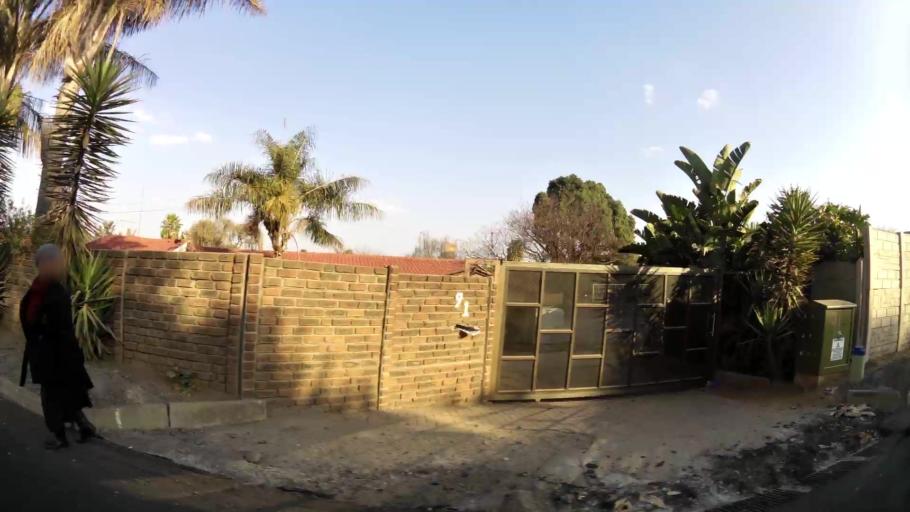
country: ZA
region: Gauteng
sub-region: City of Johannesburg Metropolitan Municipality
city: Modderfontein
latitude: -26.0702
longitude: 28.2206
